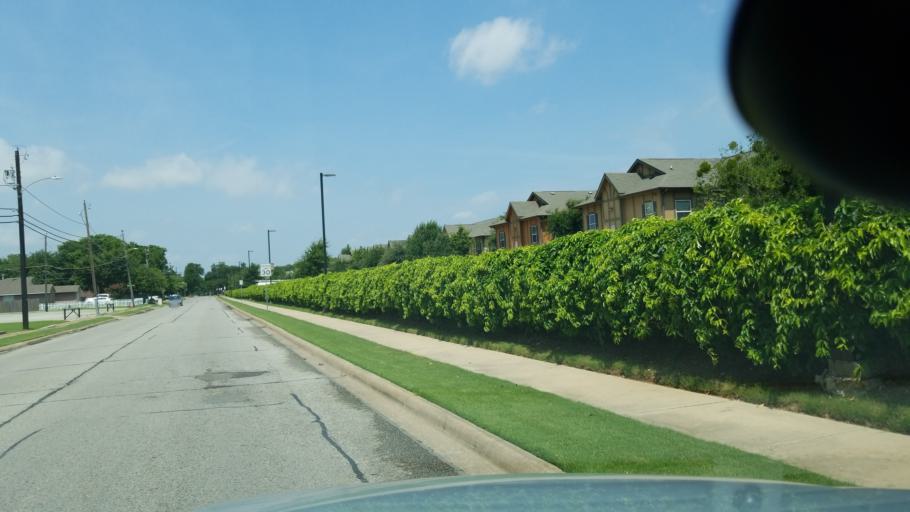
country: US
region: Texas
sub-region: Dallas County
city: Irving
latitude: 32.8333
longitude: -96.9453
